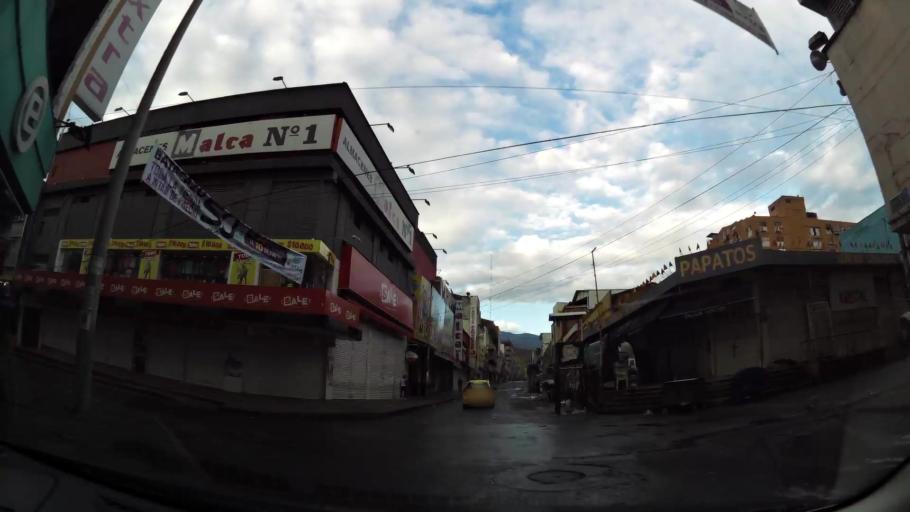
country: CO
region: Valle del Cauca
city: Cali
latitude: 3.4499
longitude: -76.5289
